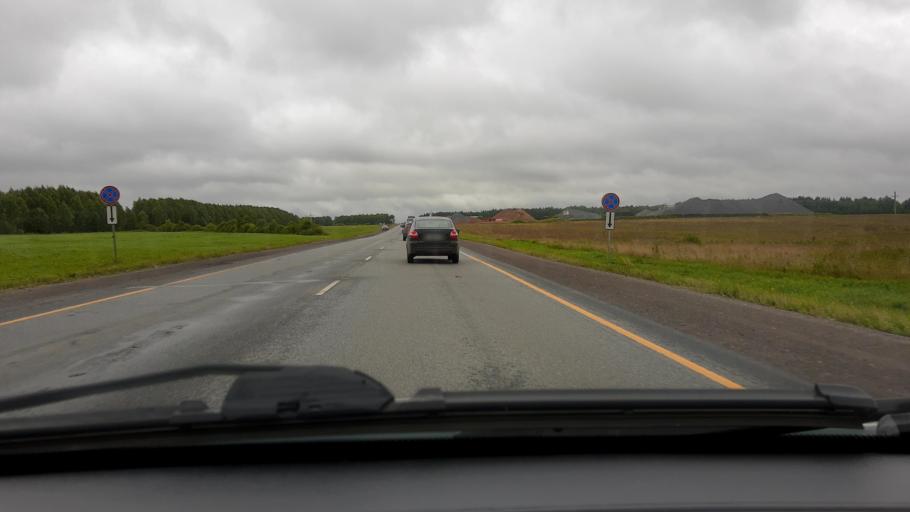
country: RU
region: Bashkortostan
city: Iglino
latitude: 54.7480
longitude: 56.3255
